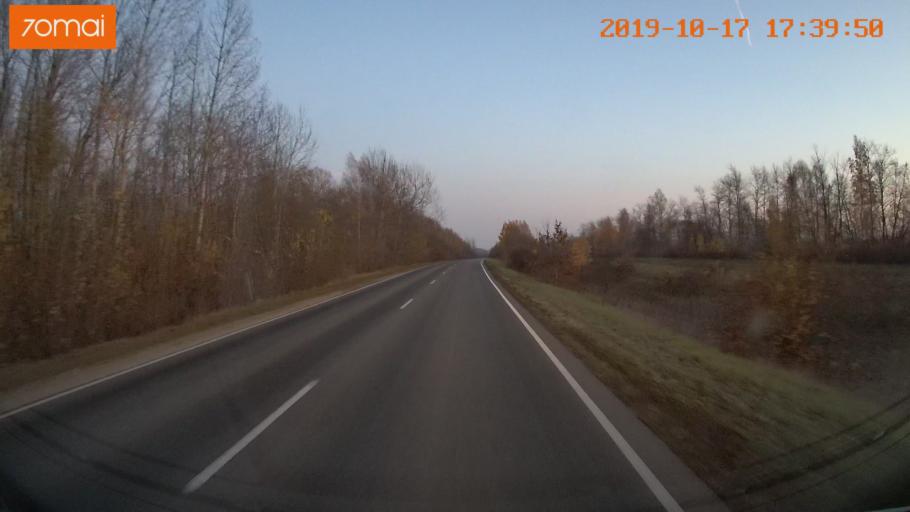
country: RU
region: Tula
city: Yepifan'
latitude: 53.7995
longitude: 38.5982
